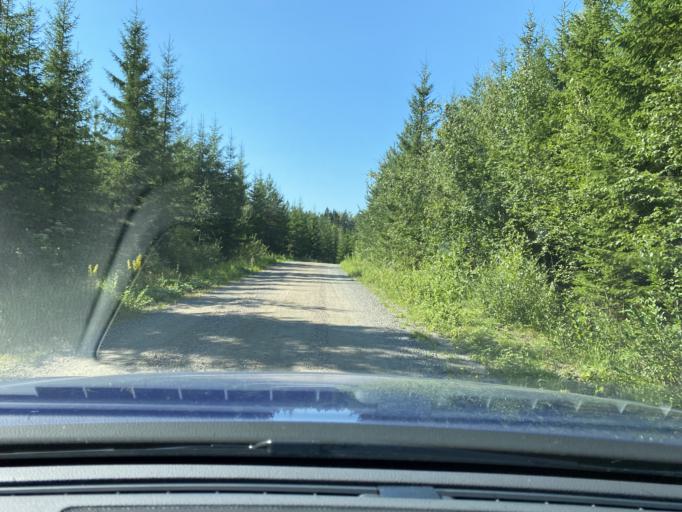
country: FI
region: Central Finland
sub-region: Jaemsae
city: Jaemsae
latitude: 61.8552
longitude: 25.3915
